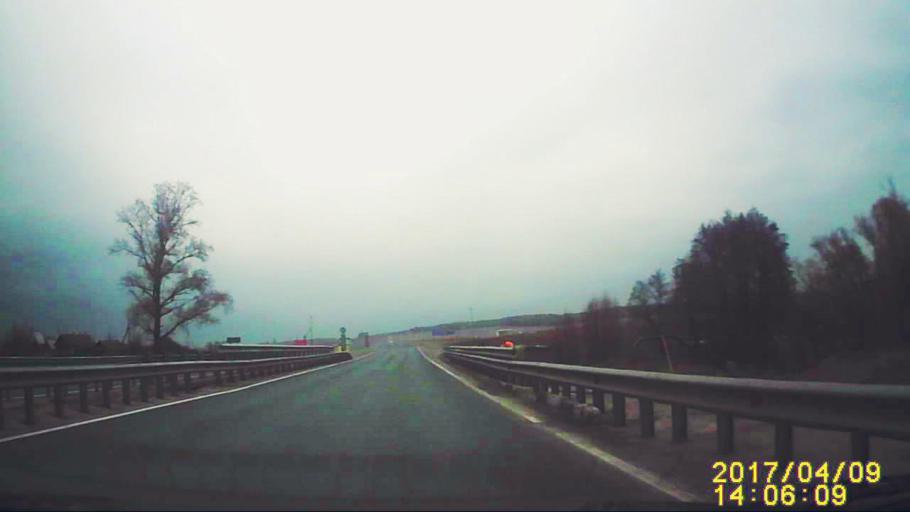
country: RU
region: Ulyanovsk
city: Silikatnyy
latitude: 54.0011
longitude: 48.2211
